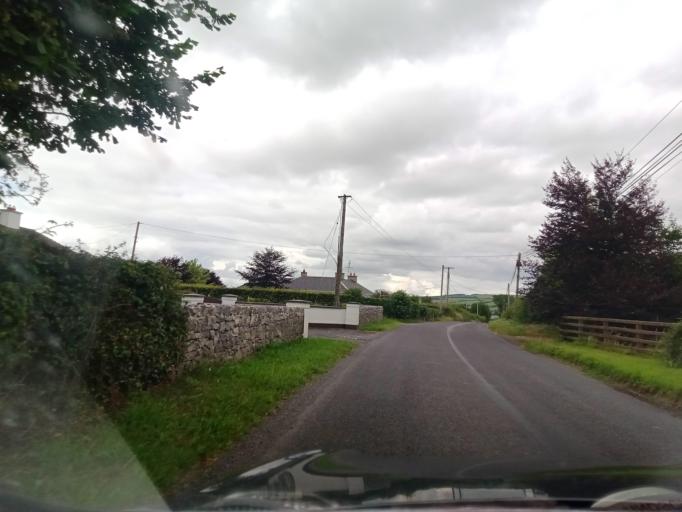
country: IE
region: Leinster
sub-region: Laois
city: Stradbally
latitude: 52.9675
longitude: -7.1891
